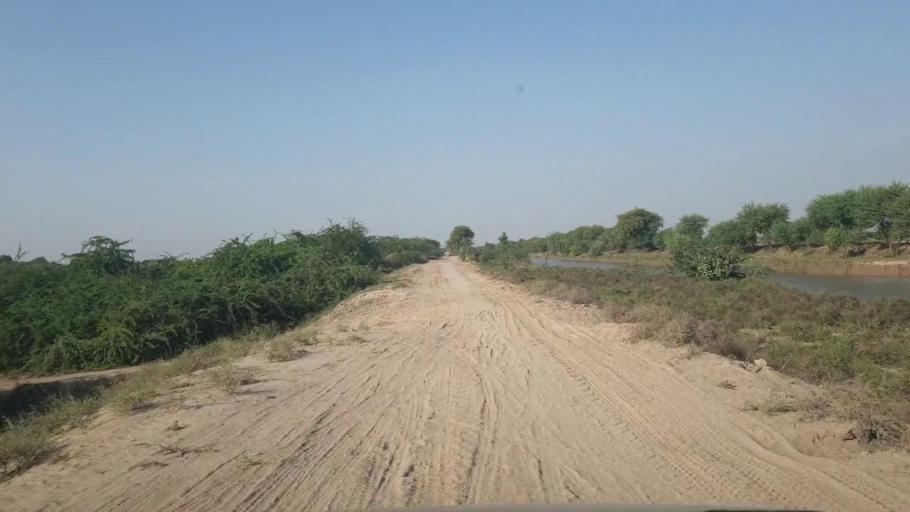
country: PK
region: Sindh
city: Badin
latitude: 24.6312
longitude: 68.8149
